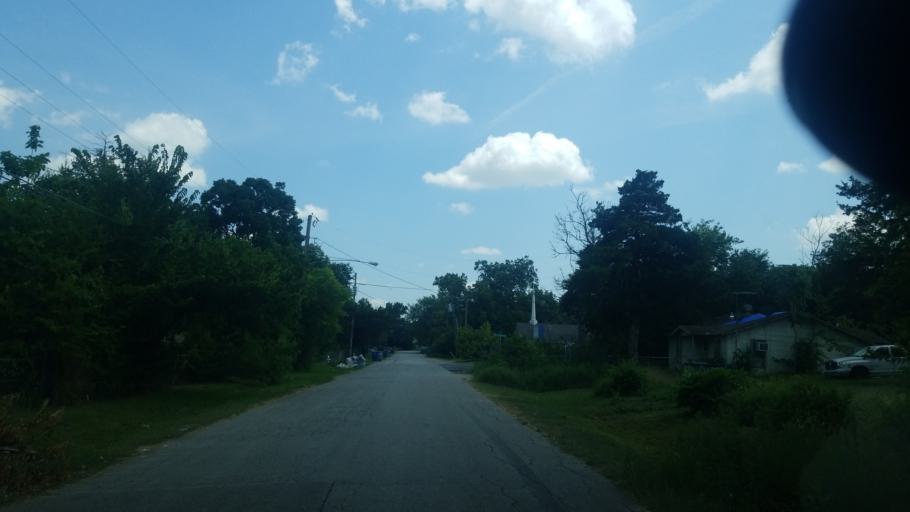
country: US
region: Texas
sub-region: Dallas County
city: Dallas
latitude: 32.7185
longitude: -96.7678
